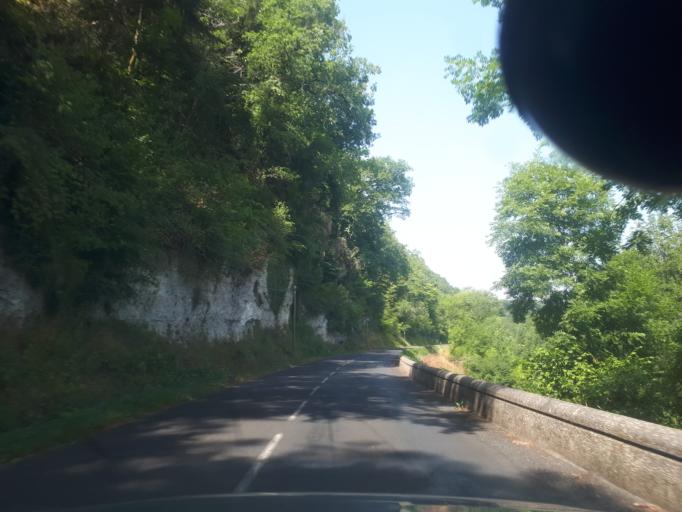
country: FR
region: Midi-Pyrenees
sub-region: Departement du Lot
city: Souillac
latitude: 44.8645
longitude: 1.4300
